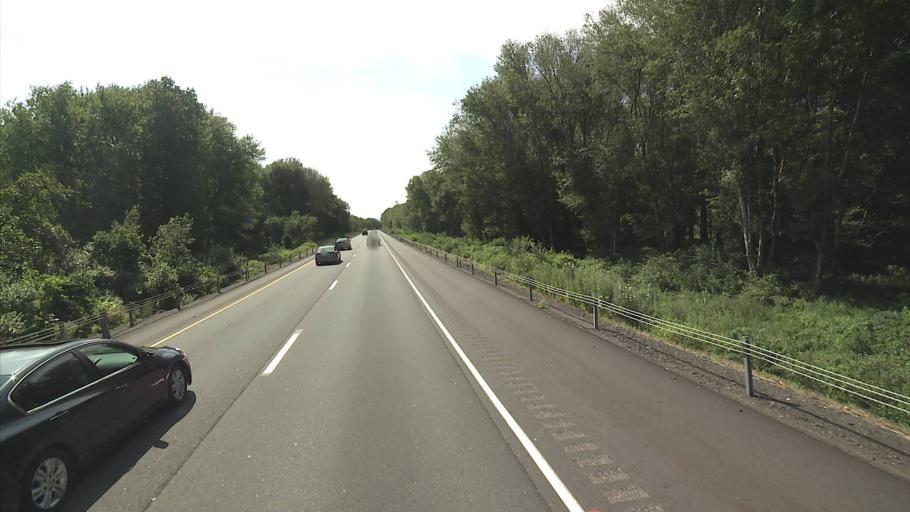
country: US
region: Connecticut
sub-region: Hartford County
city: Terramuggus
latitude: 41.6226
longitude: -72.4406
